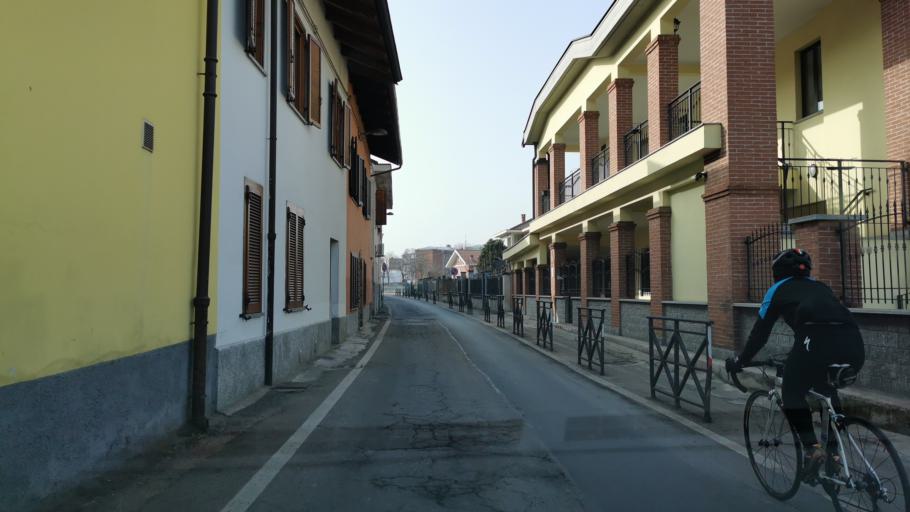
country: IT
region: Piedmont
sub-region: Provincia di Torino
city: Volpiano
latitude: 45.1994
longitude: 7.7739
